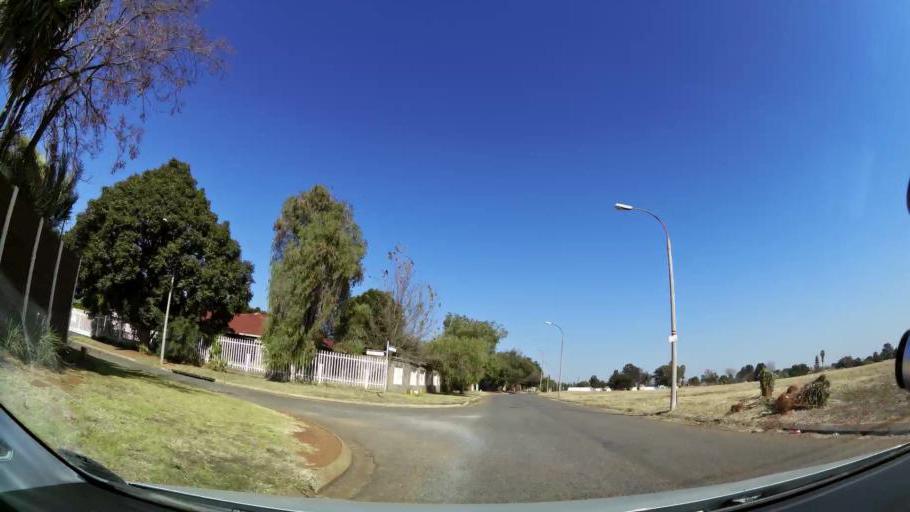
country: ZA
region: Gauteng
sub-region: City of Johannesburg Metropolitan Municipality
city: Modderfontein
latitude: -26.0516
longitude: 28.2063
